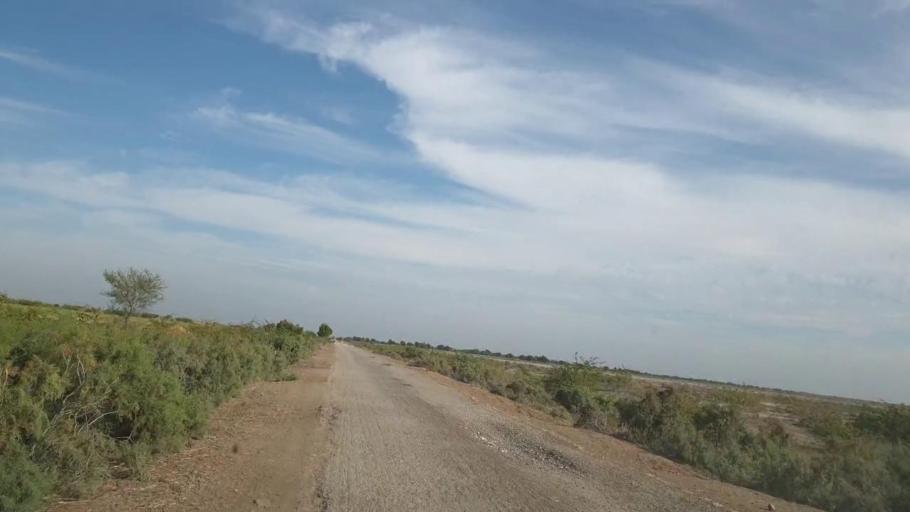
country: PK
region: Sindh
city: Pithoro
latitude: 25.6389
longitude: 69.3821
